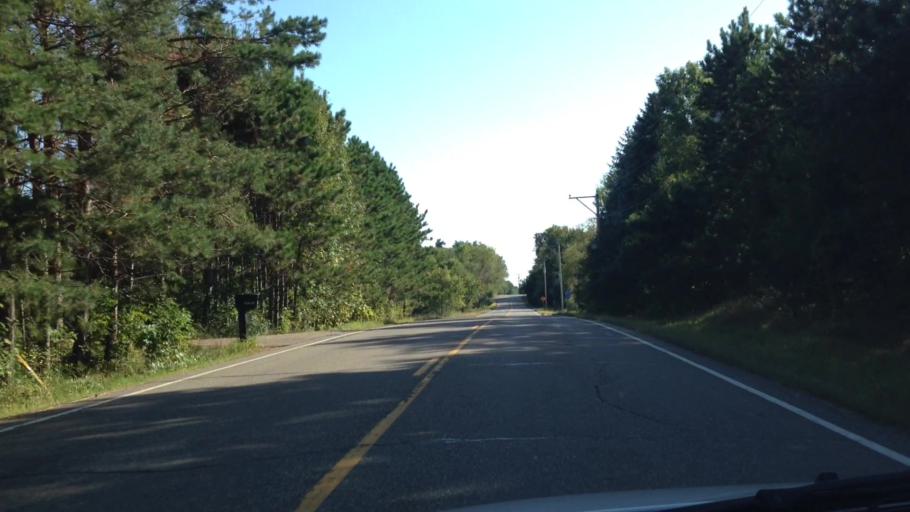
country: US
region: Minnesota
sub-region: Washington County
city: Stillwater
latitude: 45.1034
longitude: -92.8129
